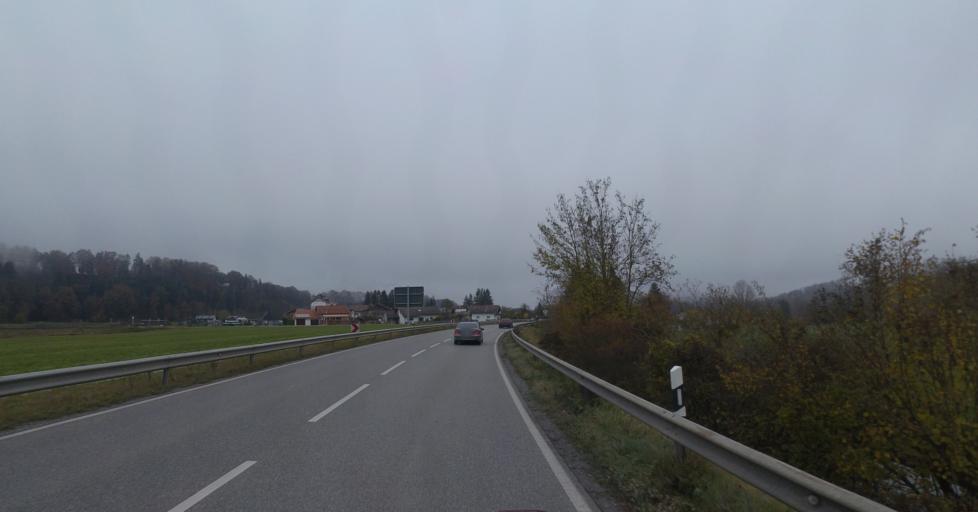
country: DE
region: Bavaria
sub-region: Upper Bavaria
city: Engelsberg
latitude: 48.1013
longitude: 12.5631
